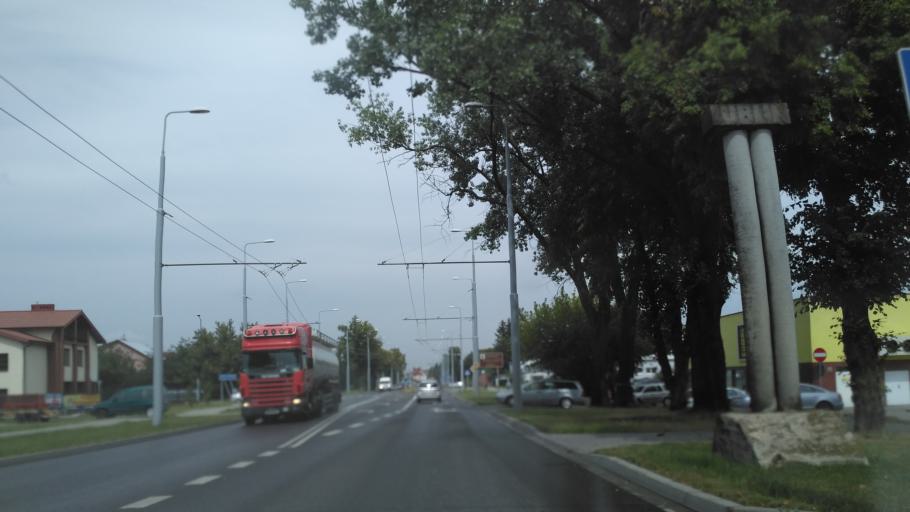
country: PL
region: Lublin Voivodeship
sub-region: Powiat lubelski
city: Lublin
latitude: 51.1997
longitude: 22.5860
